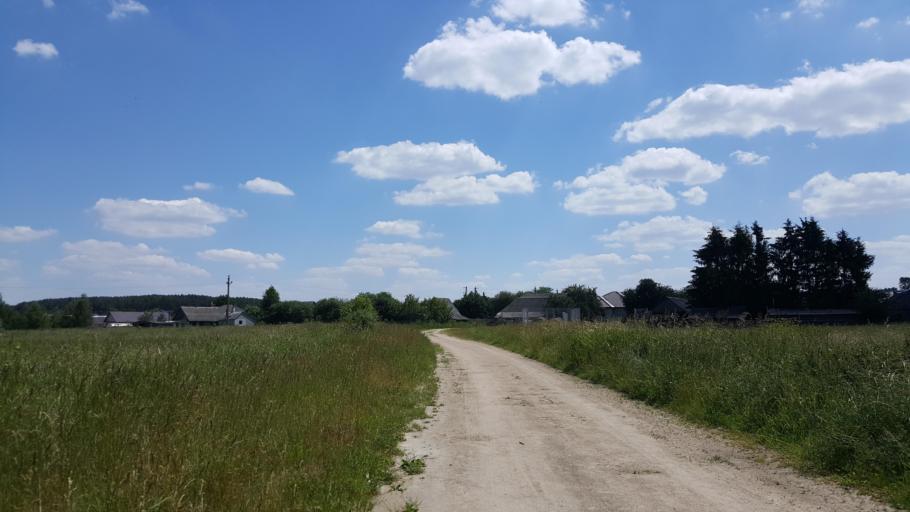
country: BY
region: Brest
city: Kamyanyets
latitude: 52.4099
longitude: 23.8283
